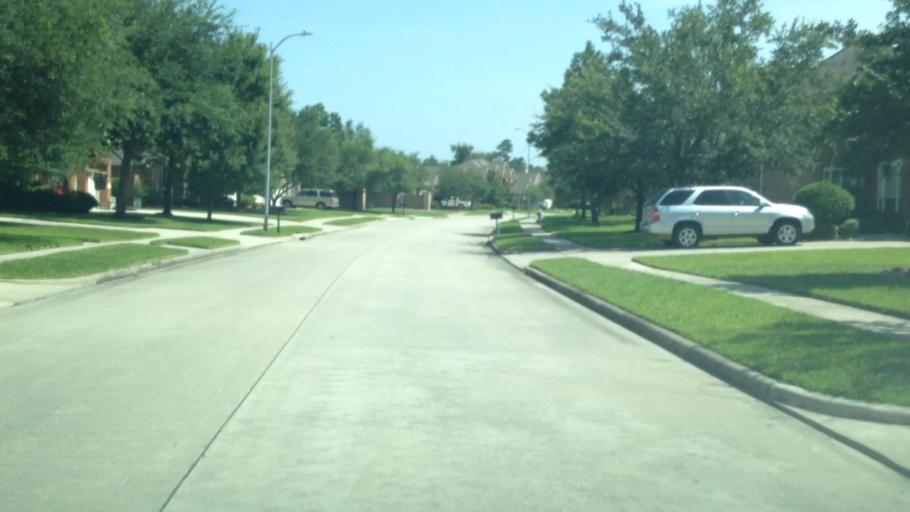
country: US
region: Texas
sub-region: Harris County
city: Sheldon
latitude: 29.9216
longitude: -95.1710
